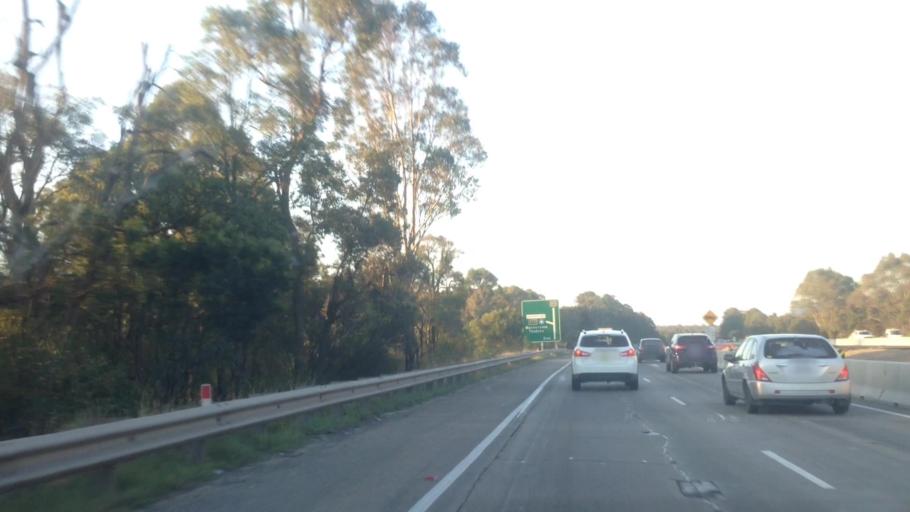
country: AU
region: New South Wales
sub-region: Wyong Shire
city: Jilliby
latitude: -33.2505
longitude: 151.4047
